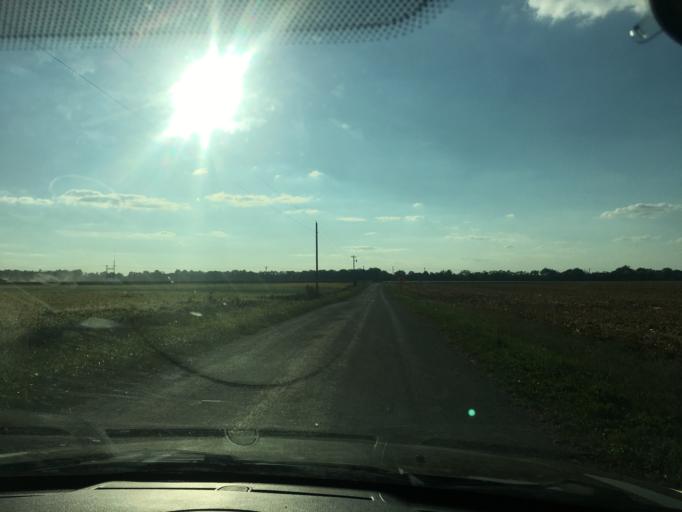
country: US
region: Ohio
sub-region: Champaign County
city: Urbana
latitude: 40.1720
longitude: -83.7795
